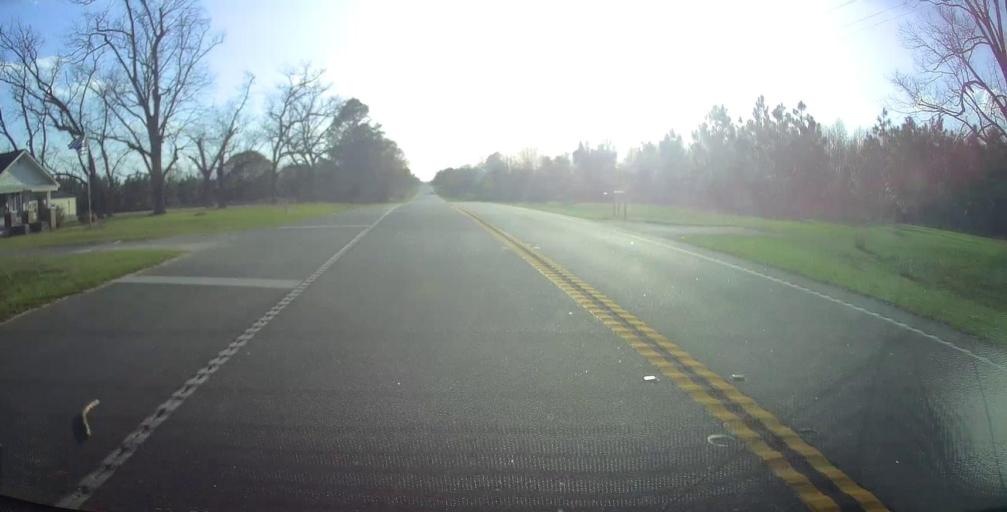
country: US
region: Georgia
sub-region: Tattnall County
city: Reidsville
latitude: 32.1158
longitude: -82.0758
